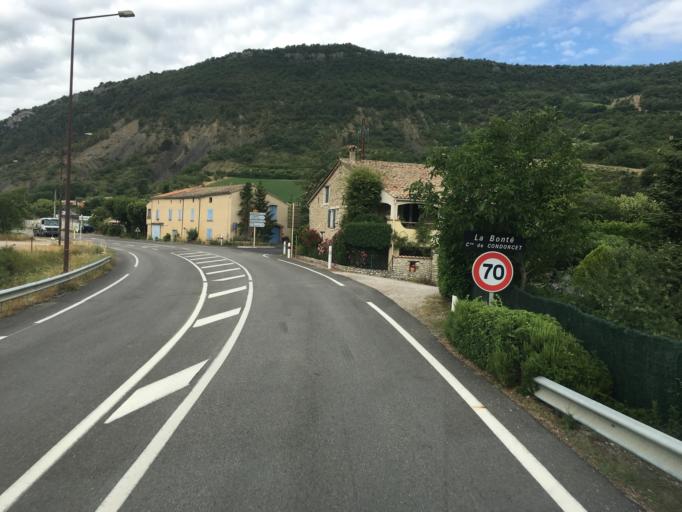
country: FR
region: Rhone-Alpes
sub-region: Departement de la Drome
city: Nyons
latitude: 44.3889
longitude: 5.1973
